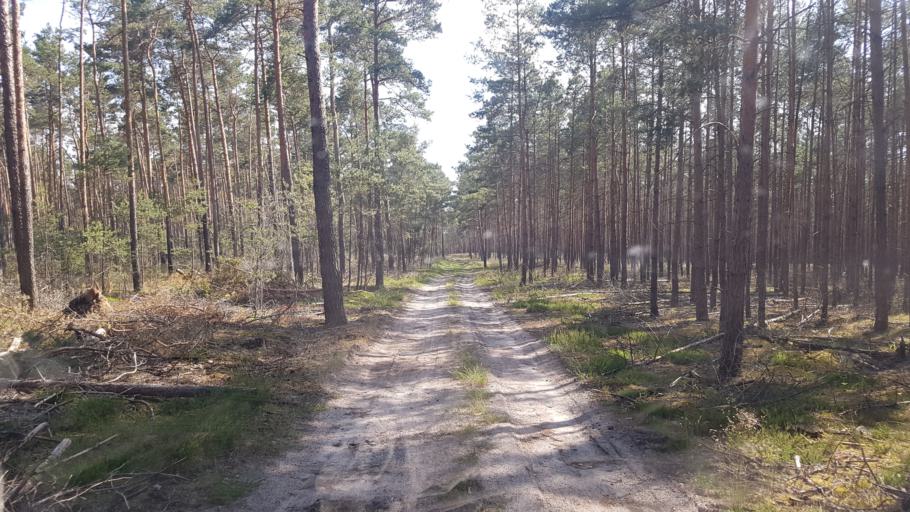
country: DE
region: Brandenburg
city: Trobitz
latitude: 51.6437
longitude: 13.4330
